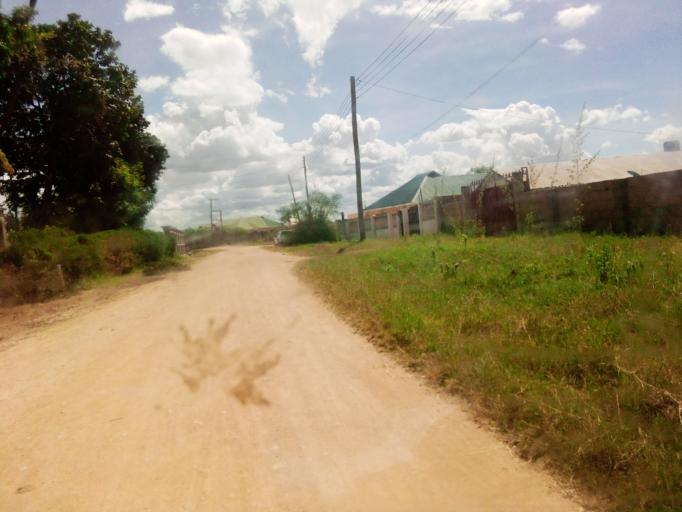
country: TZ
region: Dodoma
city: Dodoma
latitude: -6.1640
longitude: 35.7657
